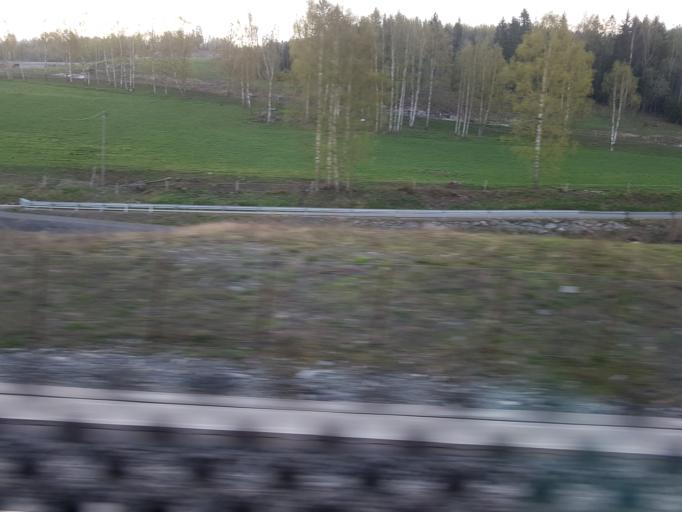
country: NO
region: Akershus
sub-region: Eidsvoll
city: Eidsvoll
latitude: 60.4917
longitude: 11.2322
